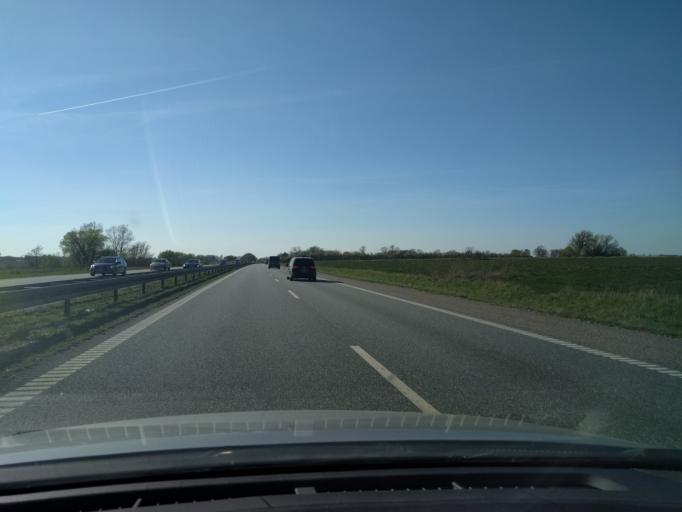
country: DK
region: South Denmark
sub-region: Nyborg Kommune
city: Nyborg
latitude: 55.3337
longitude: 10.7678
